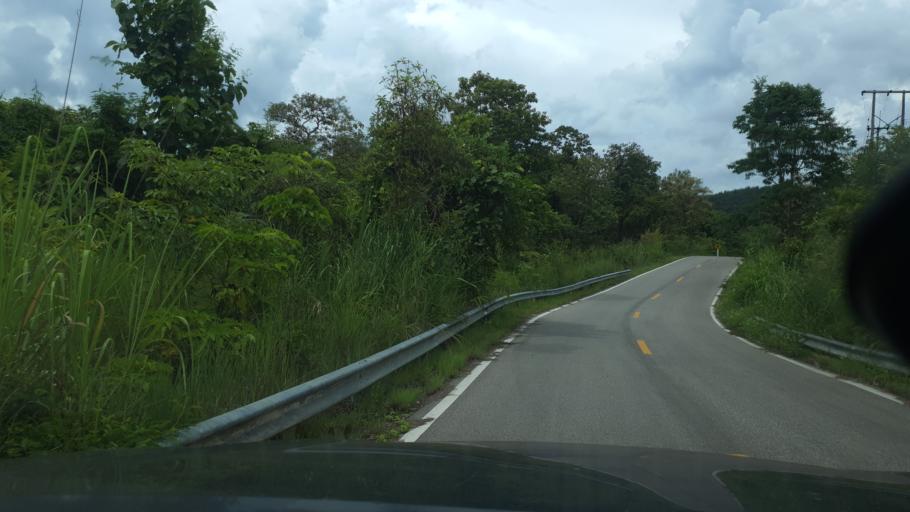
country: TH
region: Lamphun
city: Mae Tha
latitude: 18.5195
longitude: 99.2631
